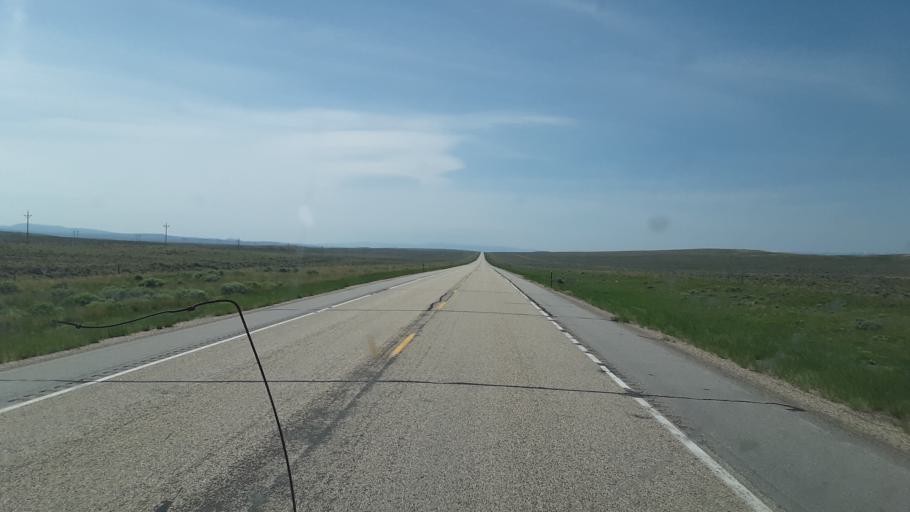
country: US
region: Wyoming
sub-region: Carbon County
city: Saratoga
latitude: 41.6031
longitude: -106.8179
